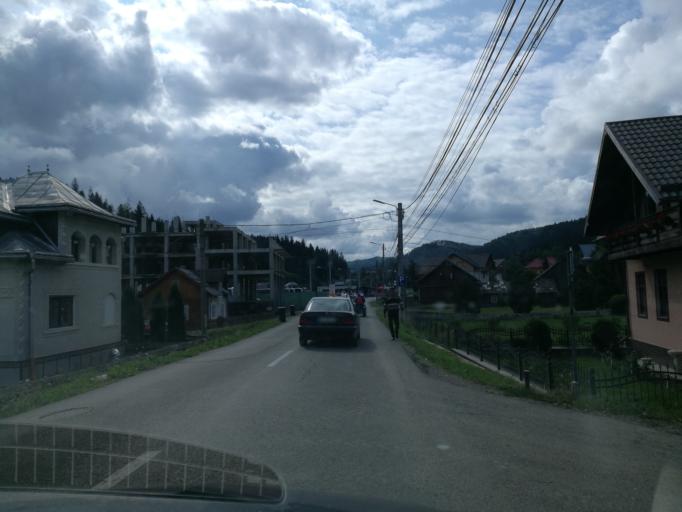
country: RO
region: Suceava
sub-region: Oras Gura Humorului
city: Gura Humorului
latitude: 47.5217
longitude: 25.8650
